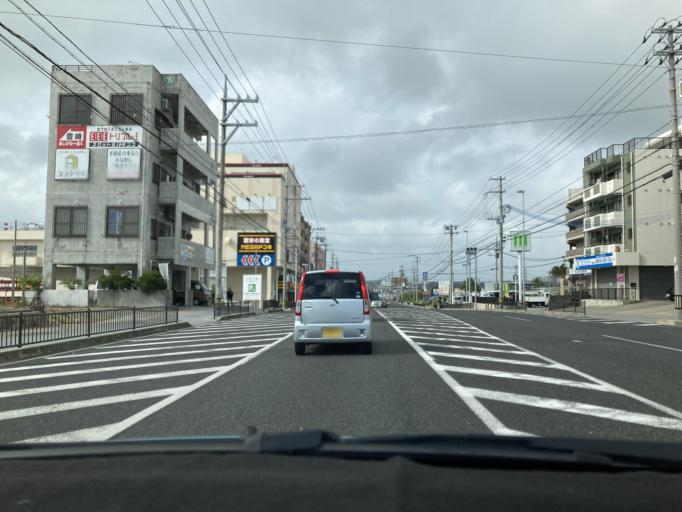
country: JP
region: Okinawa
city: Tomigusuku
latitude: 26.1602
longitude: 127.6697
